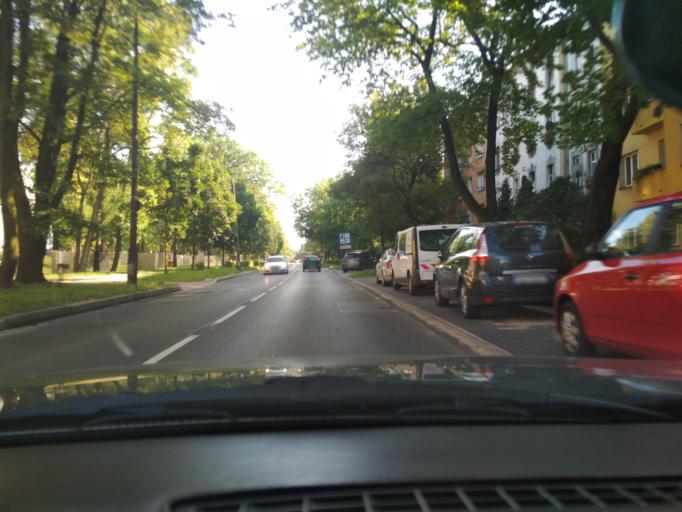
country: PL
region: Silesian Voivodeship
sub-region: Gliwice
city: Gliwice
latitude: 50.2857
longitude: 18.6639
